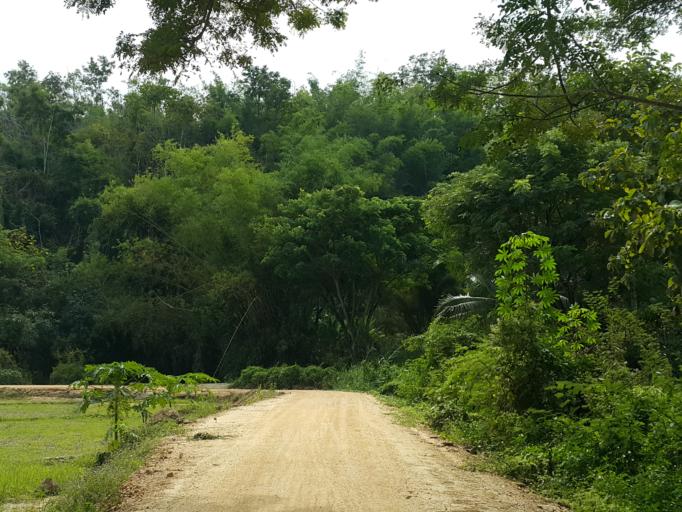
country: TH
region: Lampang
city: Hang Chat
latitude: 18.4754
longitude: 99.4072
